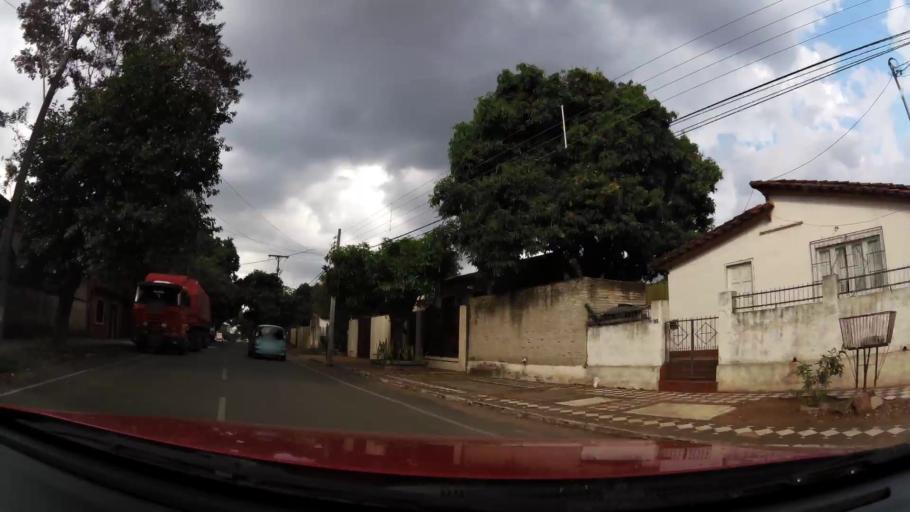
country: PY
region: Central
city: Fernando de la Mora
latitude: -25.3389
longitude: -57.5617
